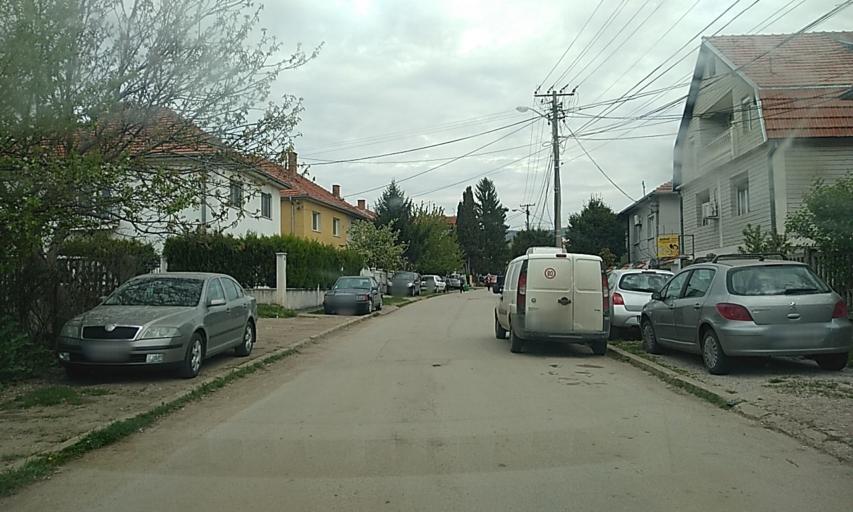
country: RS
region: Central Serbia
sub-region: Nisavski Okrug
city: Nis
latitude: 43.3315
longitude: 21.9101
